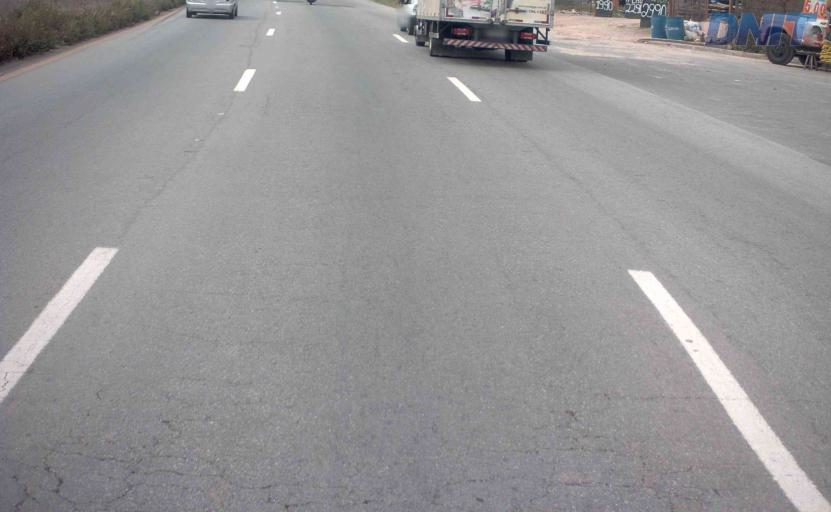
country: BR
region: Minas Gerais
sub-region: Belo Horizonte
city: Belo Horizonte
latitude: -19.8549
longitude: -43.8913
